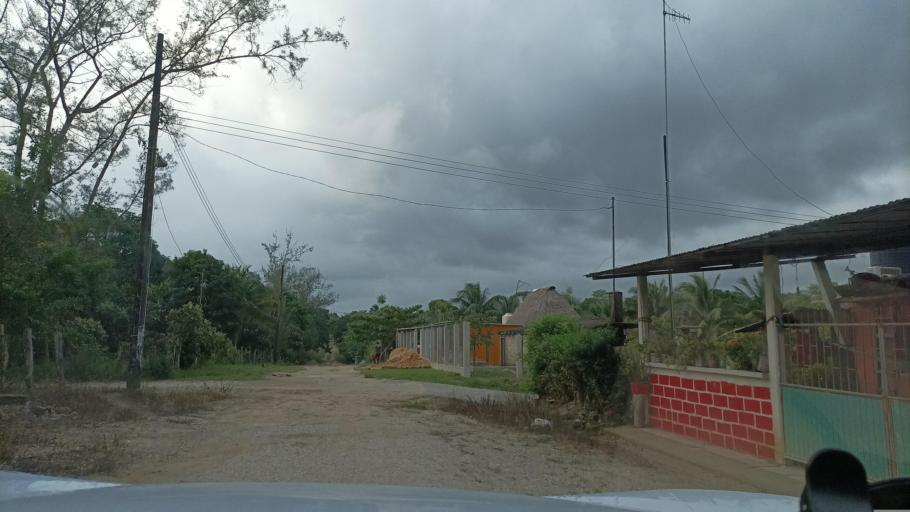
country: MX
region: Veracruz
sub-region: Moloacan
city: Cuichapa
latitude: 17.9234
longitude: -94.3662
